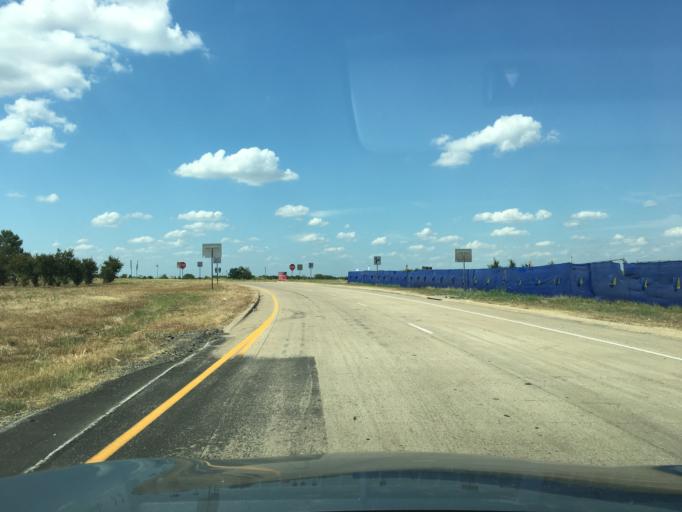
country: US
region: Texas
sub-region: Tarrant County
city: Mansfield
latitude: 32.5368
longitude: -97.1012
